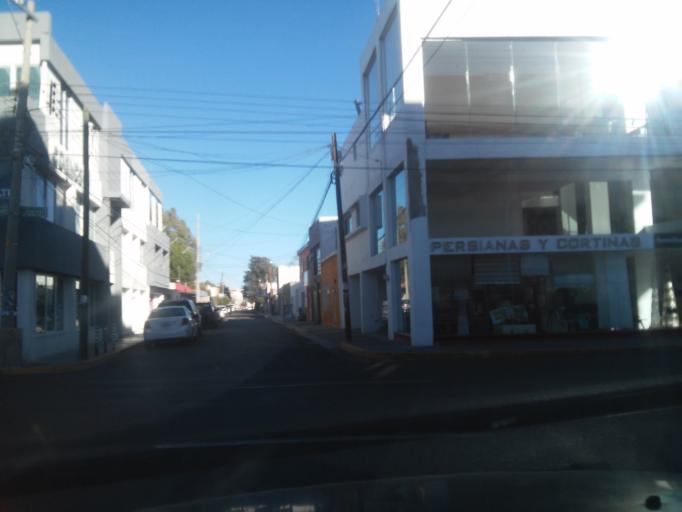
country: MX
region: Durango
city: Victoria de Durango
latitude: 24.0307
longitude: -104.6535
